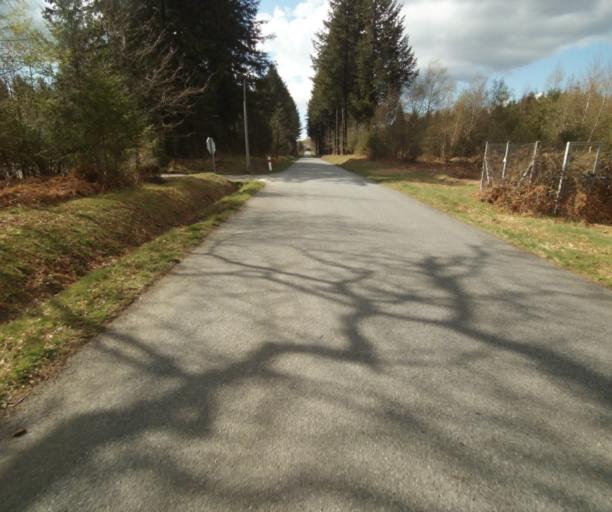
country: FR
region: Limousin
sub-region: Departement de la Correze
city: Argentat
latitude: 45.2311
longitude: 1.9350
